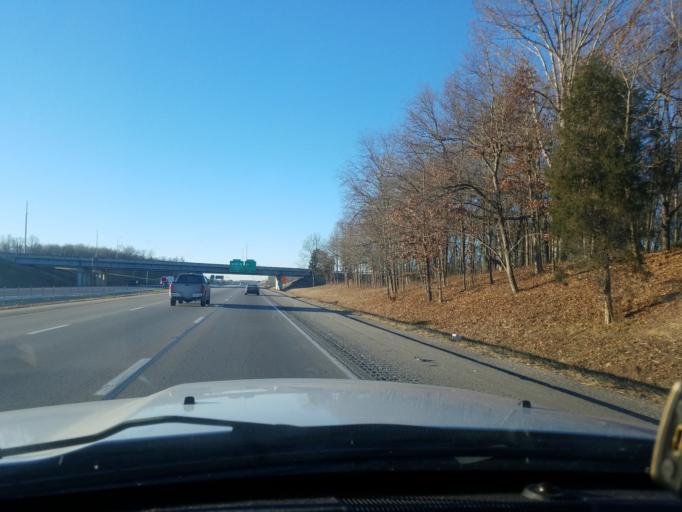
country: US
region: Kentucky
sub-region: Hardin County
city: Elizabethtown
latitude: 37.7045
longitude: -85.8327
